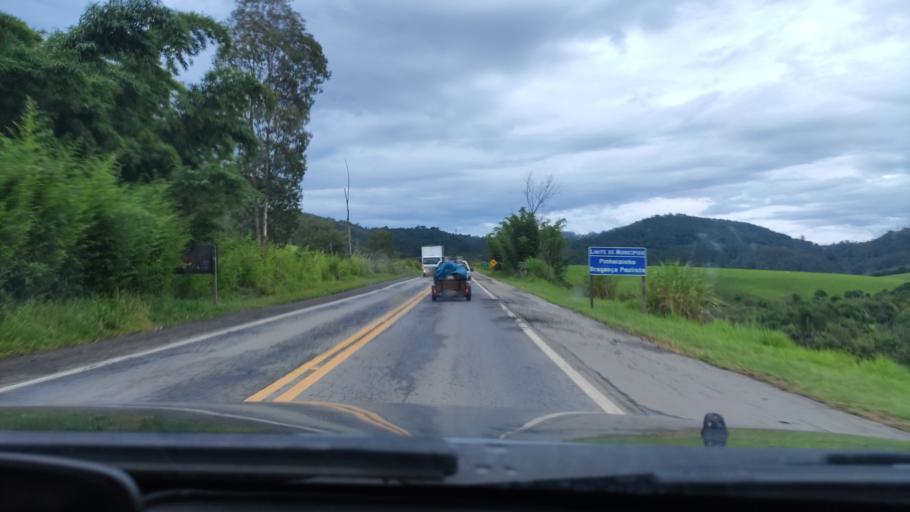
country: BR
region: Sao Paulo
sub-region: Braganca Paulista
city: Braganca Paulista
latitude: -22.8410
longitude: -46.5508
